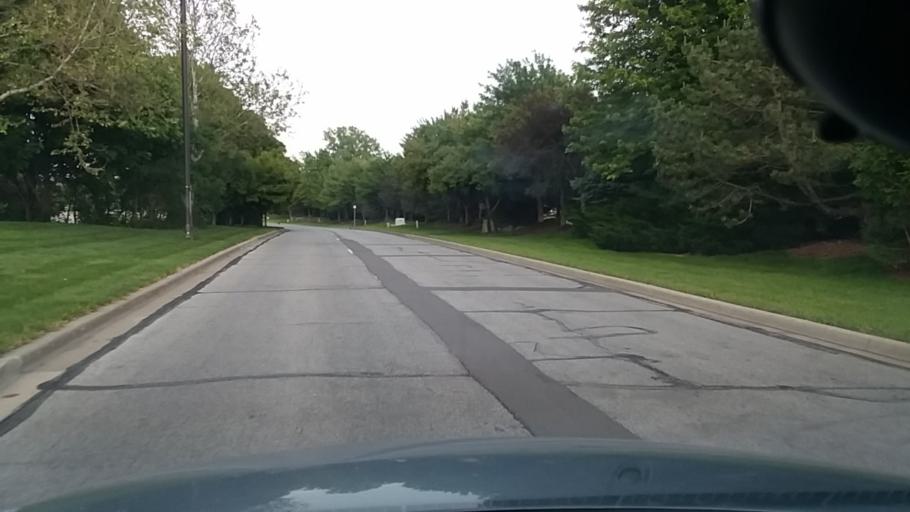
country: US
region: Kansas
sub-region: Johnson County
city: Olathe
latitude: 38.9504
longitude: -94.8157
